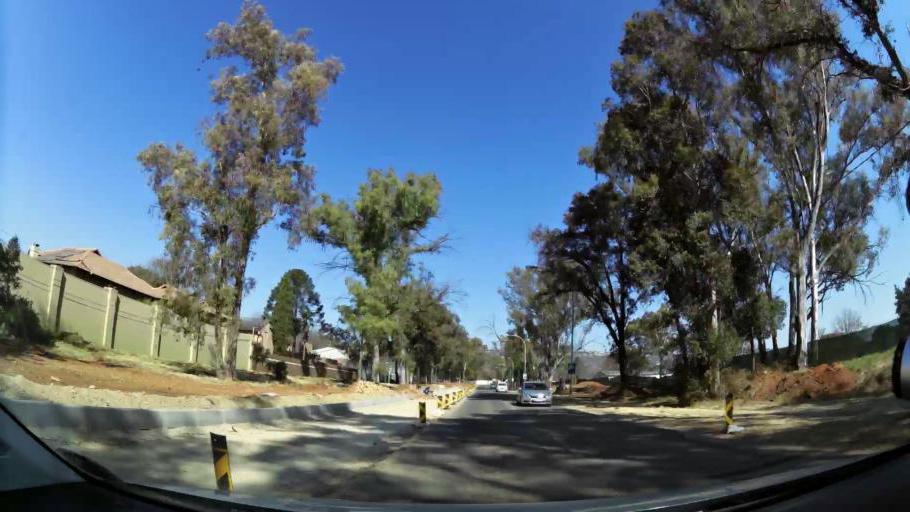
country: ZA
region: Gauteng
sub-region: City of Johannesburg Metropolitan Municipality
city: Modderfontein
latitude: -26.1541
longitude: 28.1211
